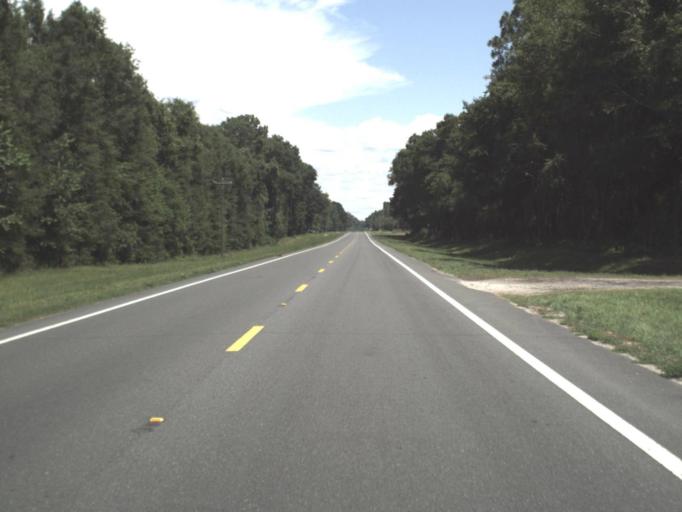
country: US
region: Florida
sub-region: Lafayette County
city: Mayo
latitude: 30.0699
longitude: -83.2013
